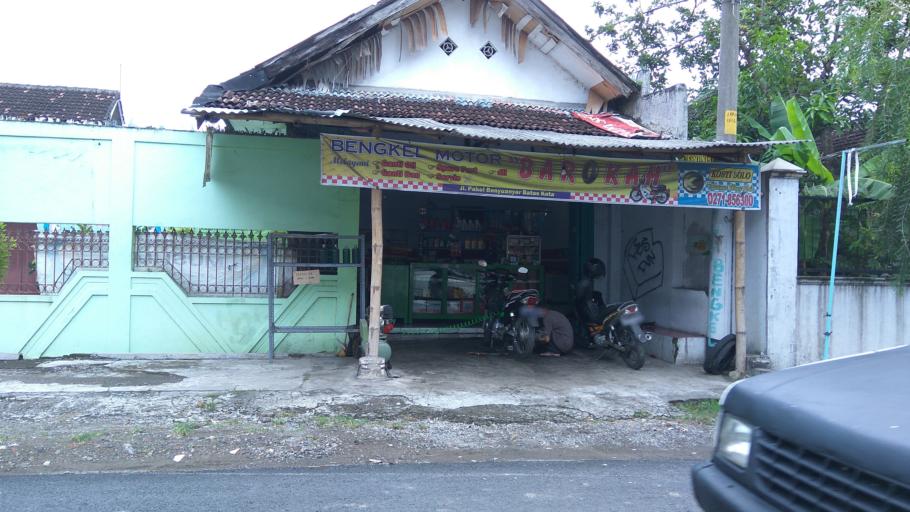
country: ID
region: Central Java
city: Surakarta
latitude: -7.5379
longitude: 110.7993
